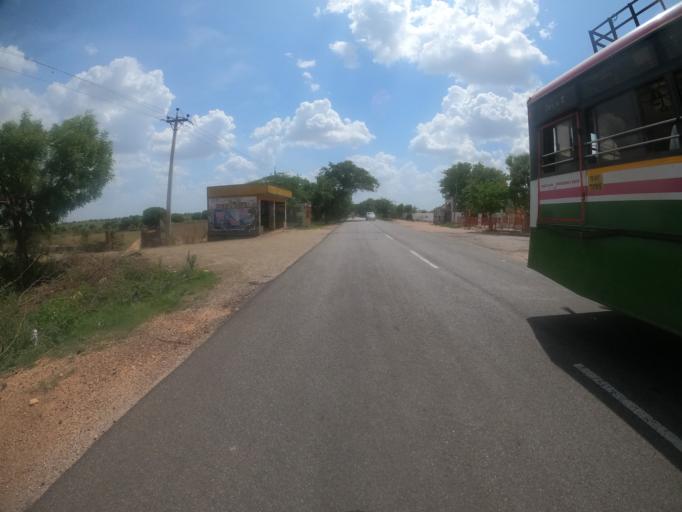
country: IN
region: Telangana
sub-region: Rangareddi
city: Sriramnagar
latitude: 17.3064
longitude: 78.1611
